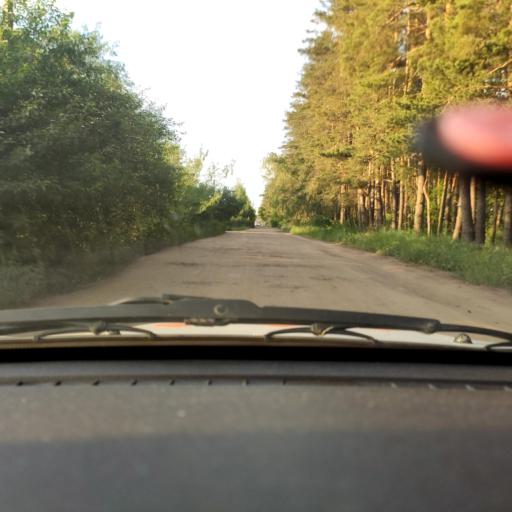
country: RU
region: Voronezj
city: Podgornoye
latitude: 51.8353
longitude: 39.1978
